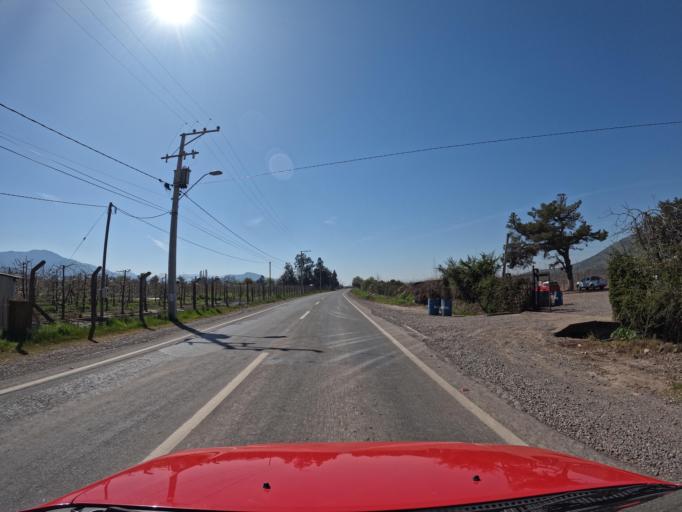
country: CL
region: Maule
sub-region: Provincia de Curico
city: Rauco
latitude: -35.0132
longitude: -71.4189
